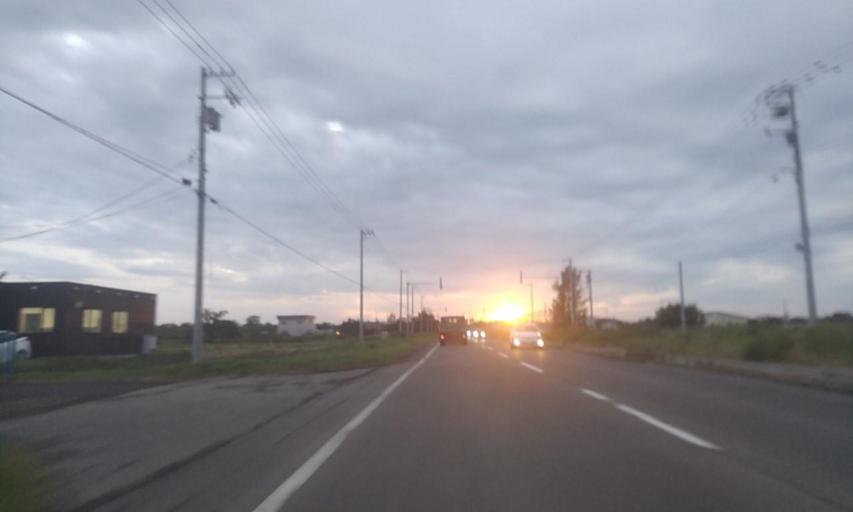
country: JP
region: Hokkaido
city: Abashiri
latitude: 43.9002
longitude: 144.6492
